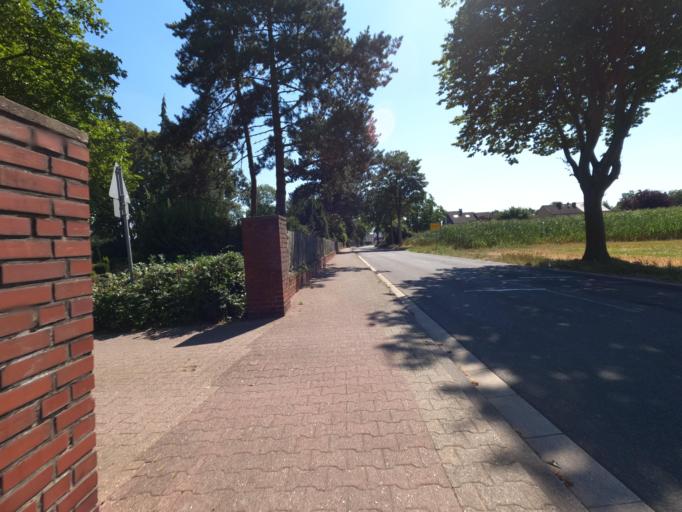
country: DE
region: North Rhine-Westphalia
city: Wegberg
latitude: 51.1044
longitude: 6.2734
